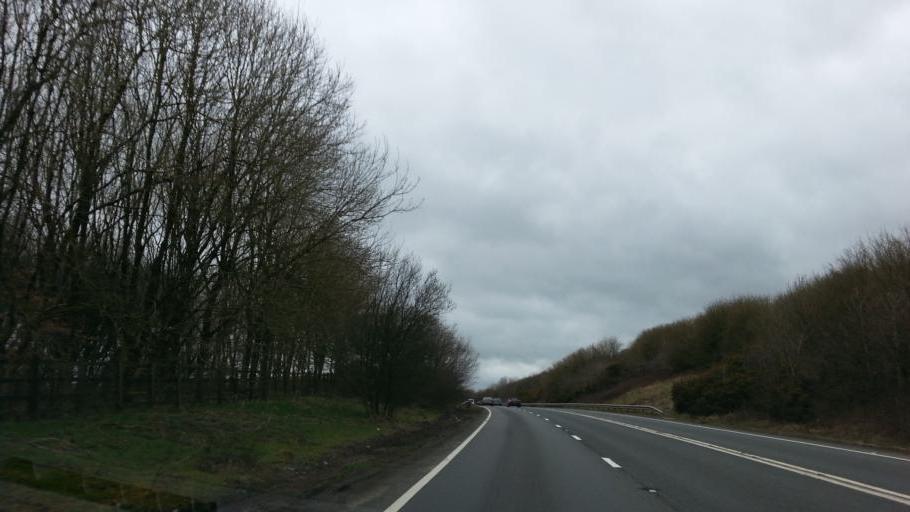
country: GB
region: England
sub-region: Devon
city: Tiverton
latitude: 50.9380
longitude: -3.5514
